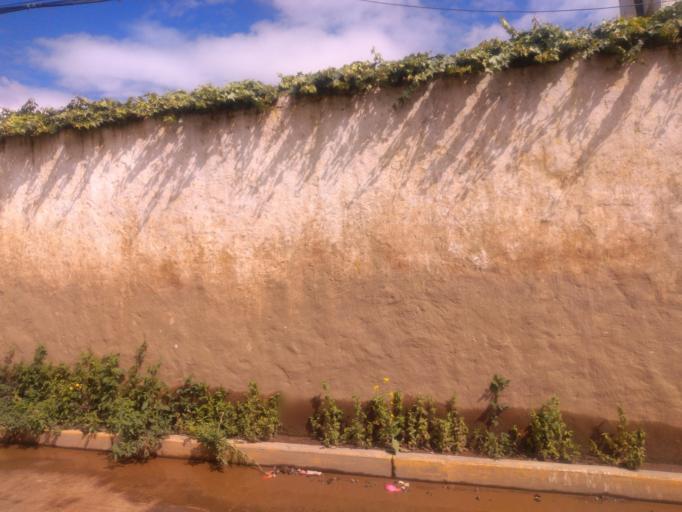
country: GT
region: Quetzaltenango
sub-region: Municipio de La Esperanza
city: La Esperanza
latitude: 14.8605
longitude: -91.5728
